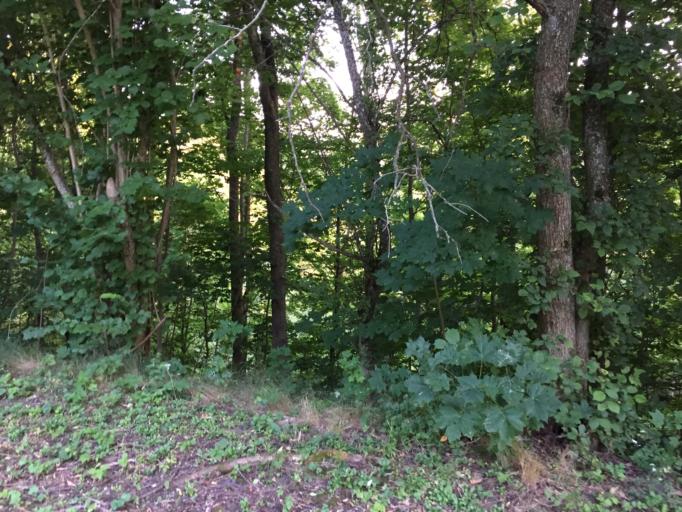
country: LV
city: Tervete
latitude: 56.4812
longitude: 23.3866
